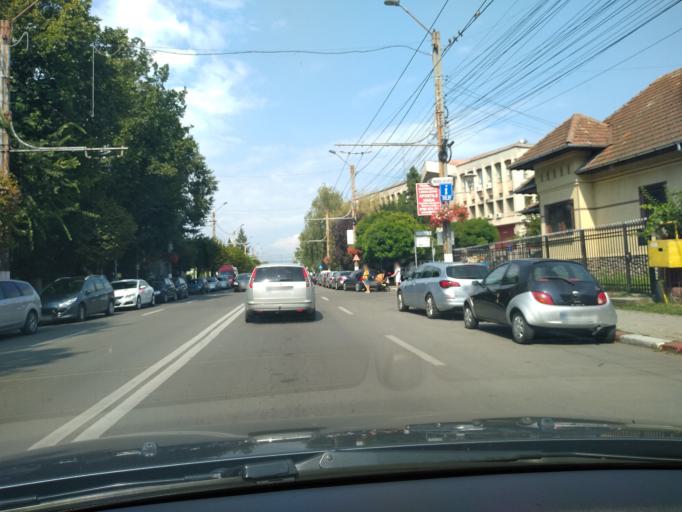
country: RO
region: Gorj
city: Targu Jiu
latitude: 45.0405
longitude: 23.2701
